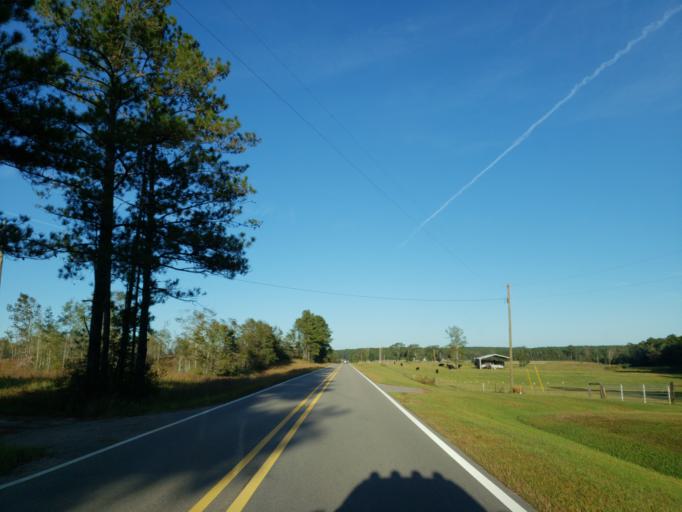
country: US
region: Mississippi
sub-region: Perry County
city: Richton
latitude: 31.3615
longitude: -88.7292
